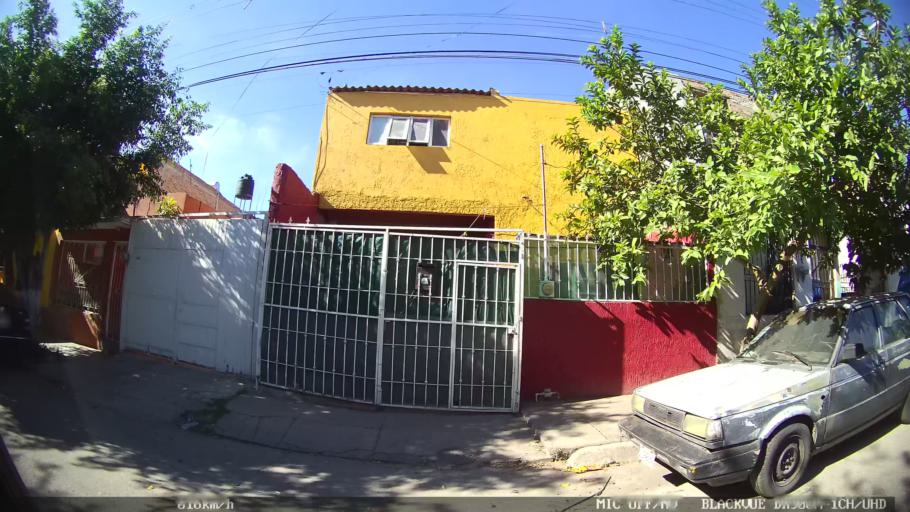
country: MX
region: Jalisco
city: Tlaquepaque
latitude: 20.6874
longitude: -103.2761
